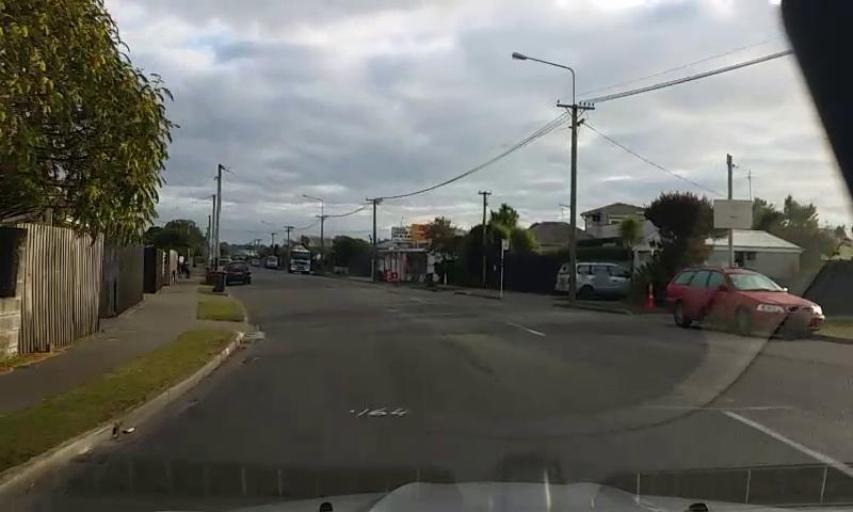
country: NZ
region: Canterbury
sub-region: Christchurch City
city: Christchurch
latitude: -43.5187
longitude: 172.7309
